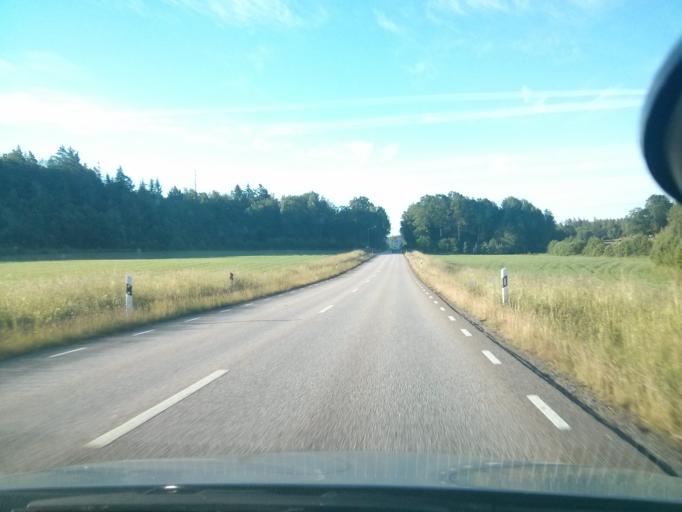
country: SE
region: Blekinge
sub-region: Ronneby Kommun
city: Brakne-Hoby
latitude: 56.3051
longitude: 15.1893
